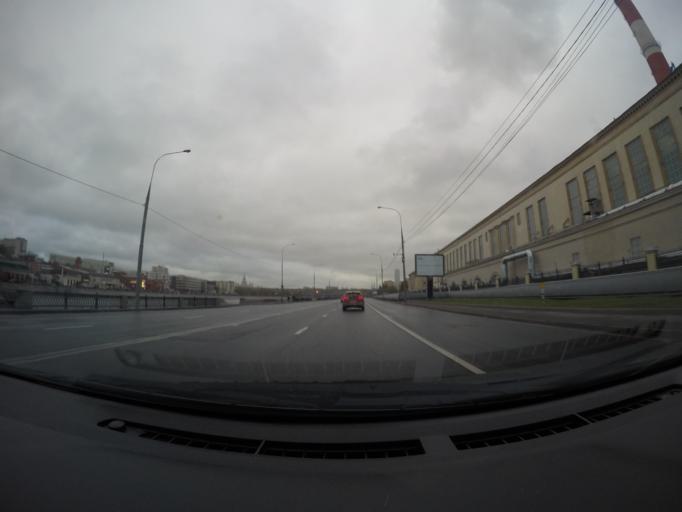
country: RU
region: Moskovskaya
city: Dorogomilovo
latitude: 55.7355
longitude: 37.5619
